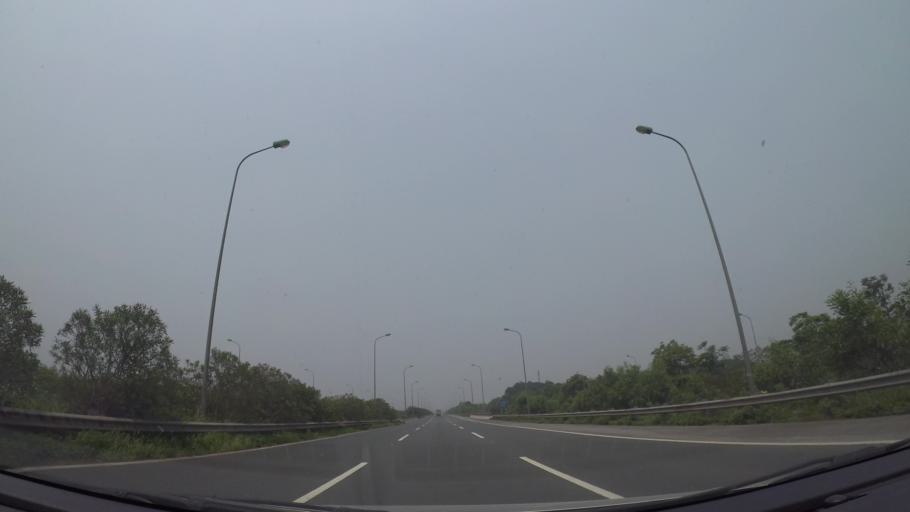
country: VN
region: Ha Noi
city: Lien Quan
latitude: 20.9897
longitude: 105.5626
